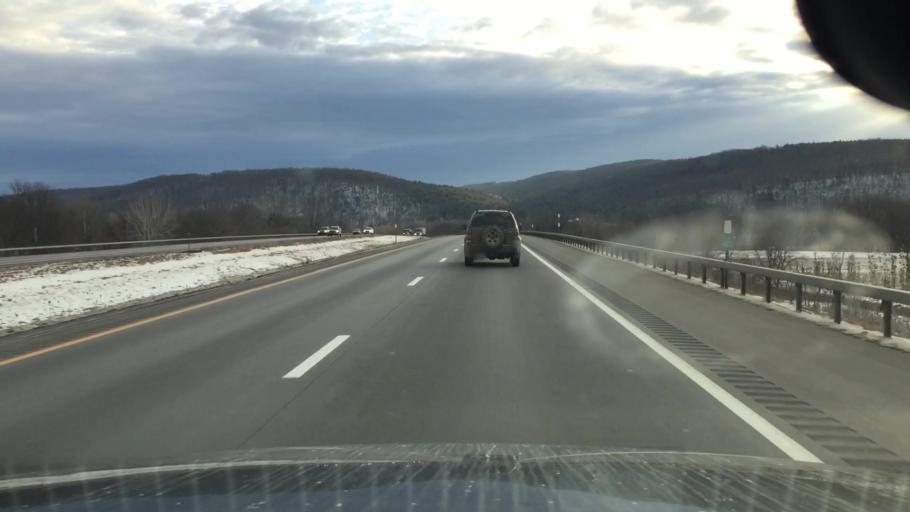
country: US
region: Pennsylvania
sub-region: Bradford County
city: Sayre
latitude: 42.0069
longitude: -76.4767
